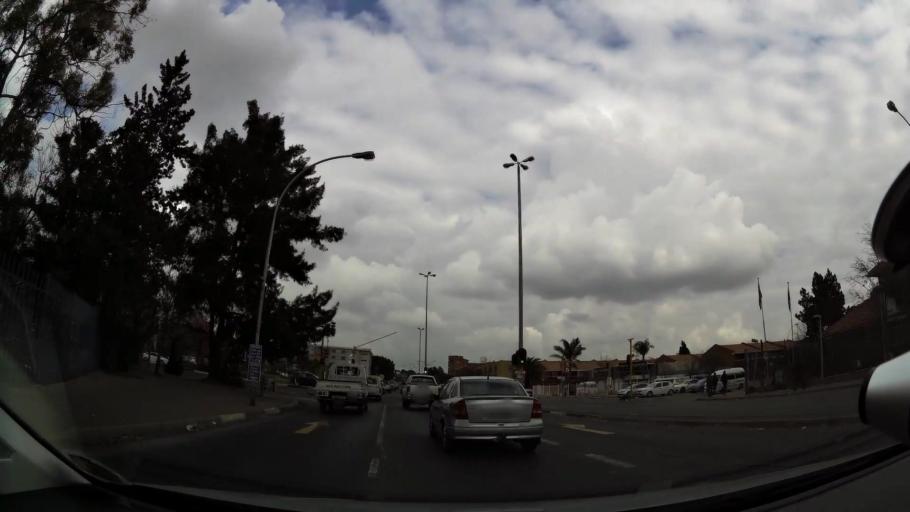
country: ZA
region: Orange Free State
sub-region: Mangaung Metropolitan Municipality
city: Bloemfontein
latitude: -29.1209
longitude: 26.2124
